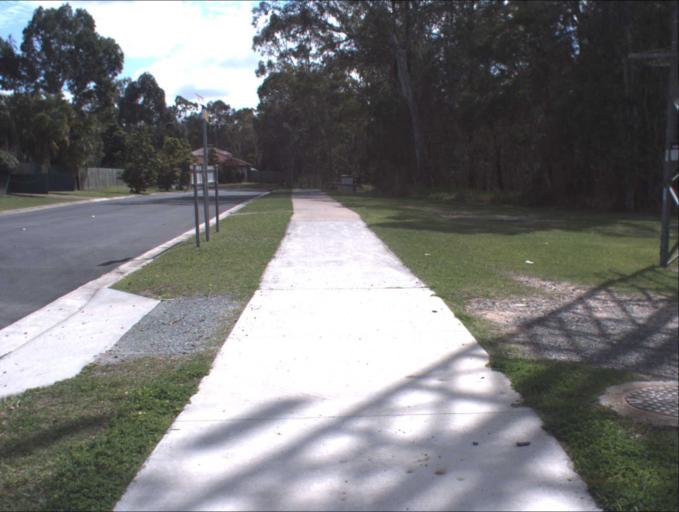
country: AU
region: Queensland
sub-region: Logan
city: Woodridge
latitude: -27.6685
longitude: 153.0596
